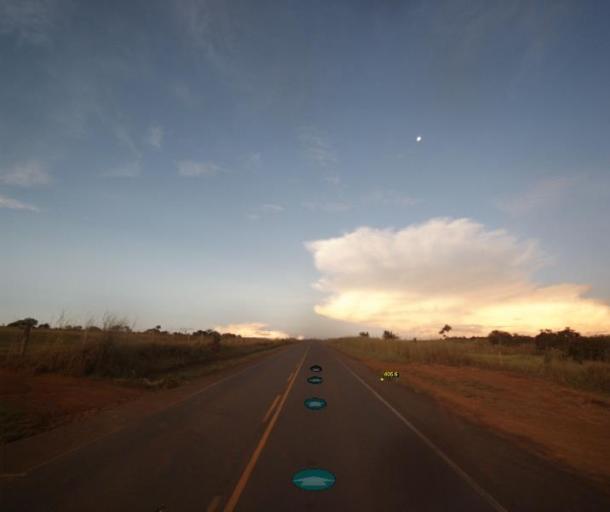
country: BR
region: Goias
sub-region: Pirenopolis
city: Pirenopolis
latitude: -16.0241
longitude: -48.8419
